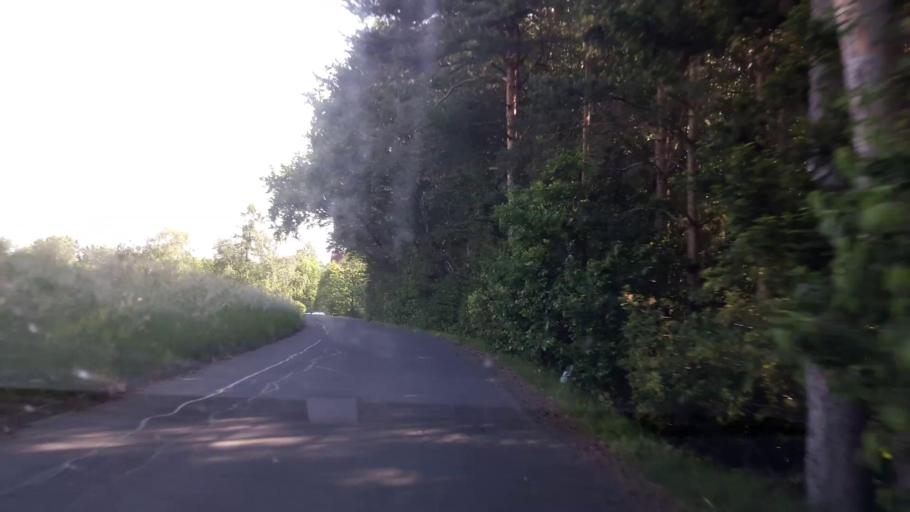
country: AT
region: Styria
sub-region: Politischer Bezirk Suedoststeiermark
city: Unterlamm
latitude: 46.9769
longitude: 16.0768
